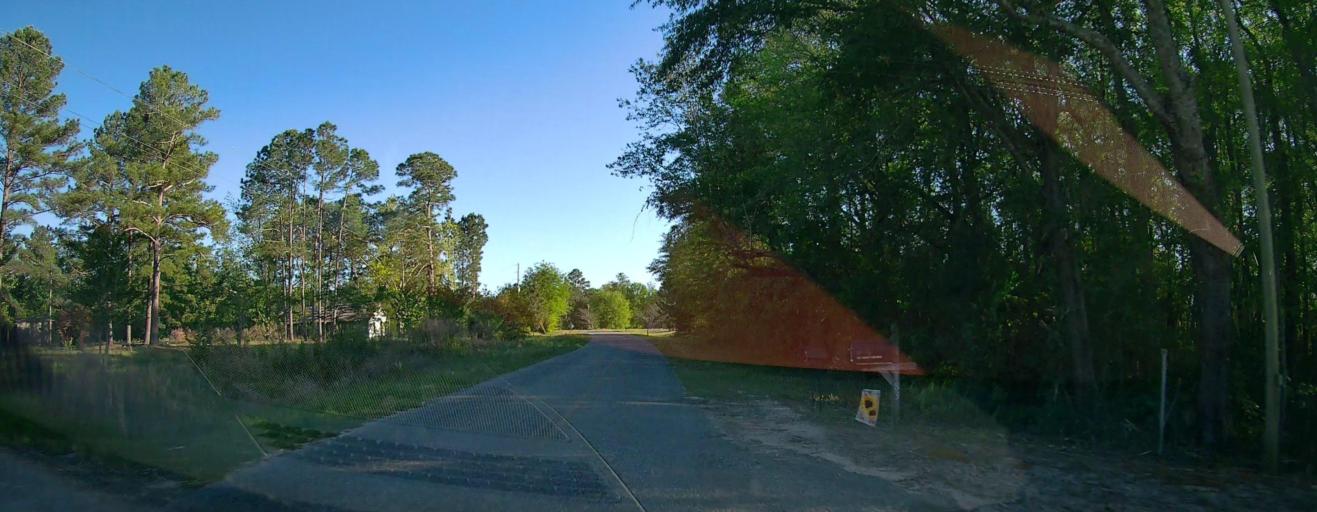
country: US
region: Georgia
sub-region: Ben Hill County
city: Fitzgerald
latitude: 31.6909
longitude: -83.1537
